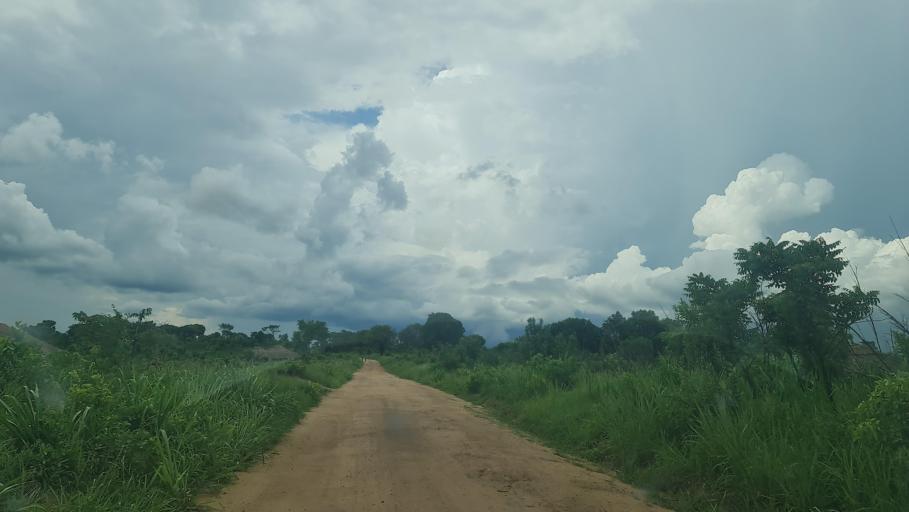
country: MW
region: Southern Region
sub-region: Nsanje District
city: Nsanje
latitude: -17.5836
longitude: 35.6655
